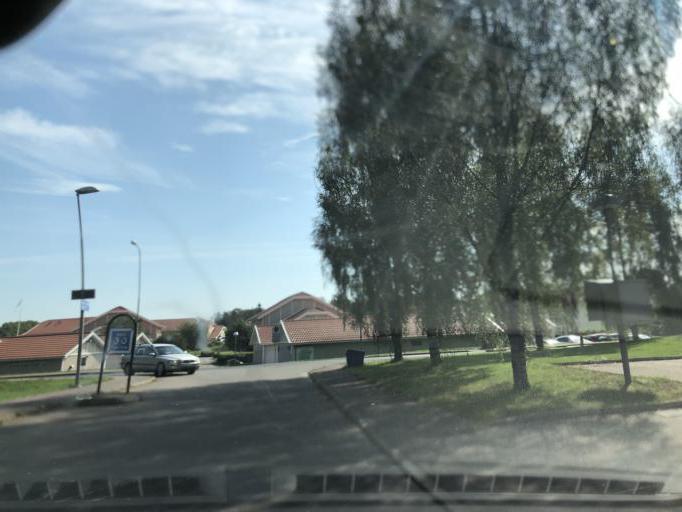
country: SE
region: Vaestra Goetaland
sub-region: Goteborg
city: Goeteborg
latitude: 57.7633
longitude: 11.9693
